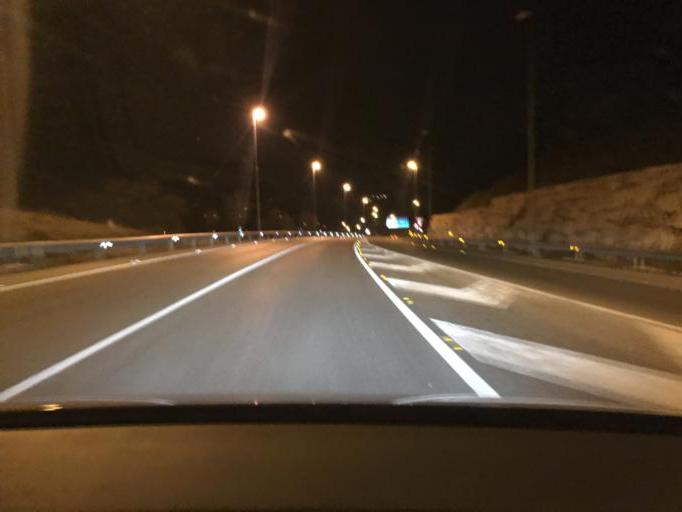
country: ES
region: Andalusia
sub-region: Provincia de Jaen
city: Jaen
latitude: 37.7808
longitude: -3.7535
